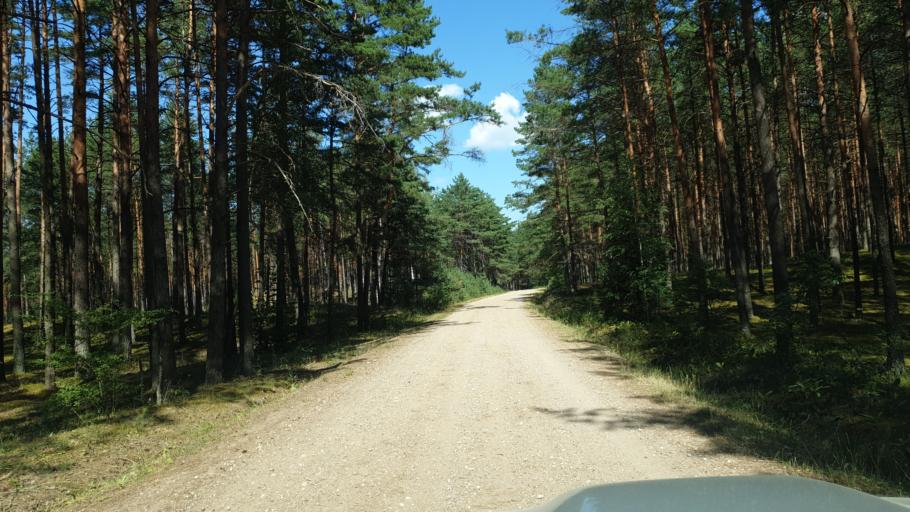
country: LT
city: Sirvintos
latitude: 54.8923
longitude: 24.9564
